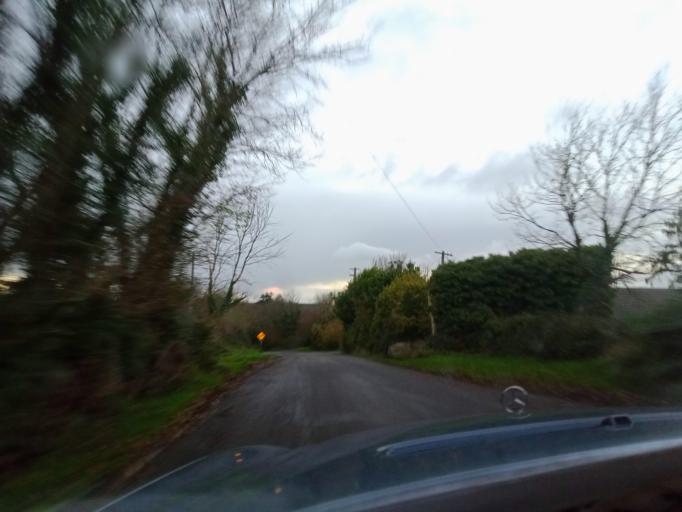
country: IE
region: Munster
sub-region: Waterford
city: Waterford
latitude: 52.3417
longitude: -7.0475
